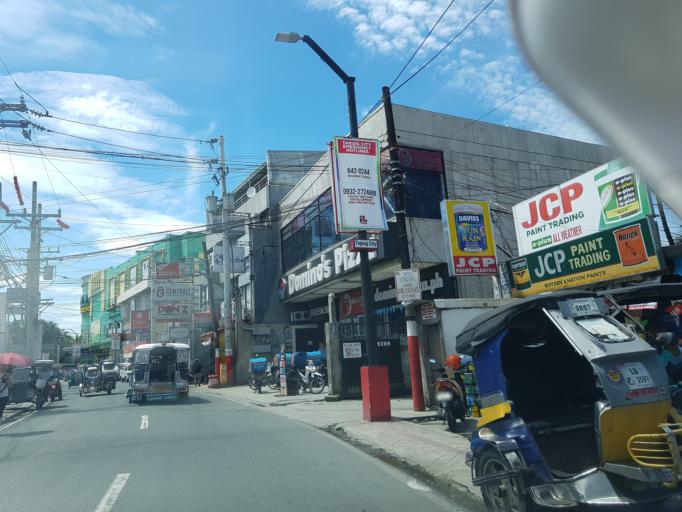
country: PH
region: Calabarzon
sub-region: Province of Rizal
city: Pateros
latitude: 14.5309
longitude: 121.0695
